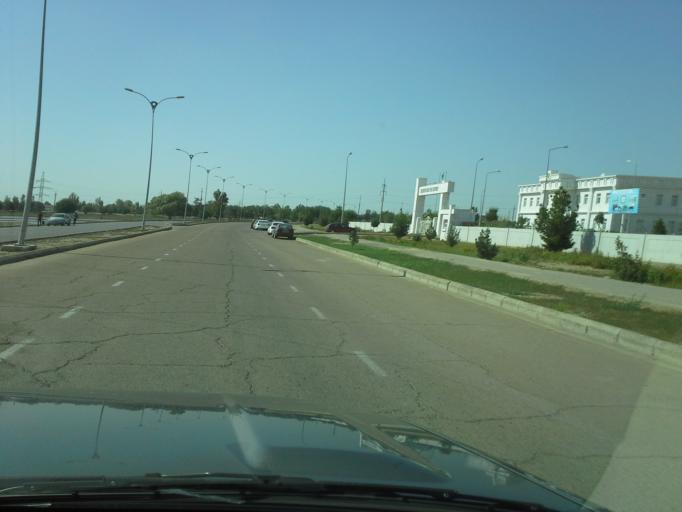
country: TM
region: Dasoguz
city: Dasoguz
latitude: 41.8098
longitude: 59.9962
